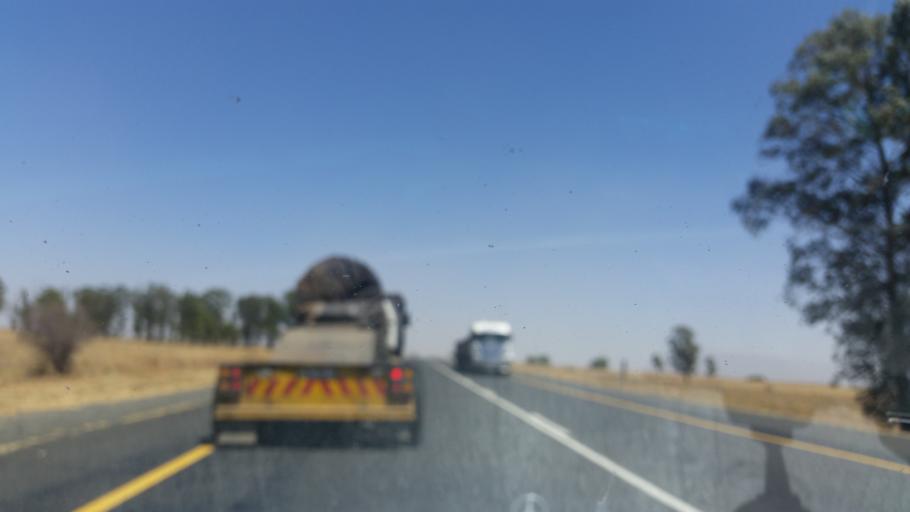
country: ZA
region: Orange Free State
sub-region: Lejweleputswa District Municipality
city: Winburg
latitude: -28.6410
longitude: 26.8898
